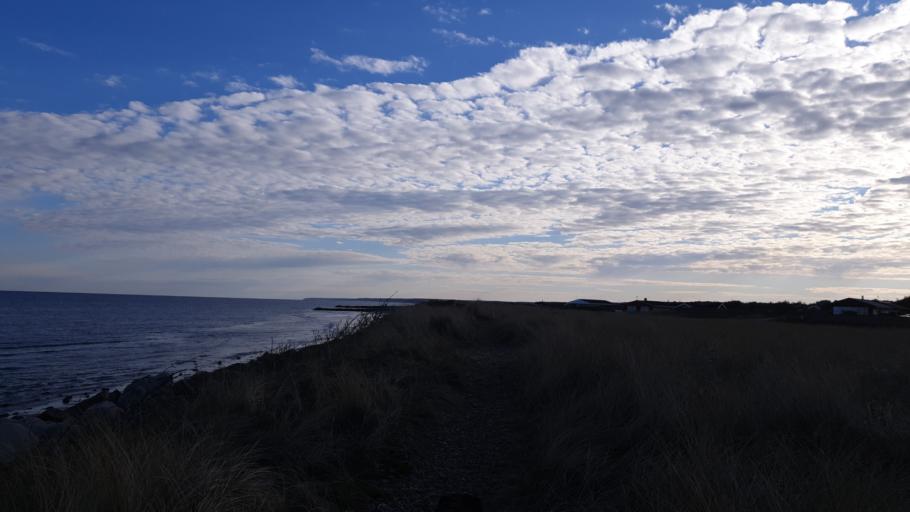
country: DK
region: North Denmark
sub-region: Hjorring Kommune
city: Hjorring
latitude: 57.4883
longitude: 9.8180
